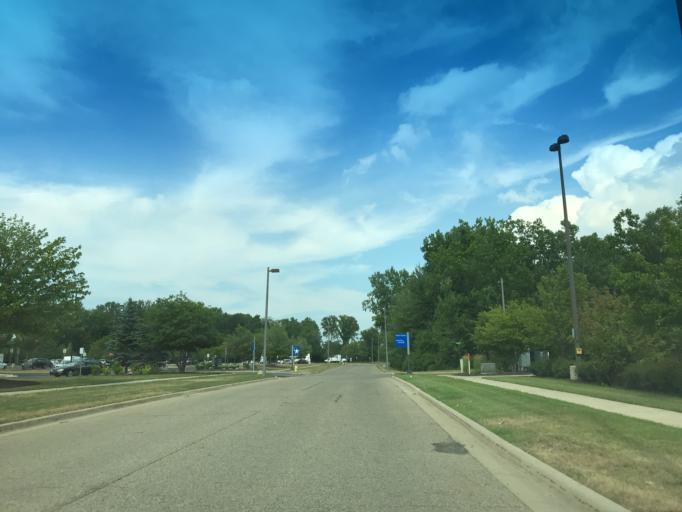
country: US
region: Michigan
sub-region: Eaton County
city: Waverly
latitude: 42.7166
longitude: -84.6311
